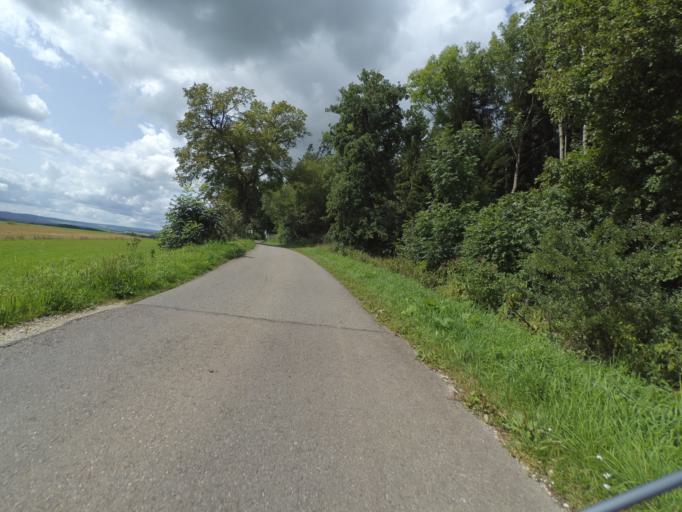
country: DE
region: Baden-Wuerttemberg
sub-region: Freiburg Region
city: Hufingen
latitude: 47.8923
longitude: 8.4690
